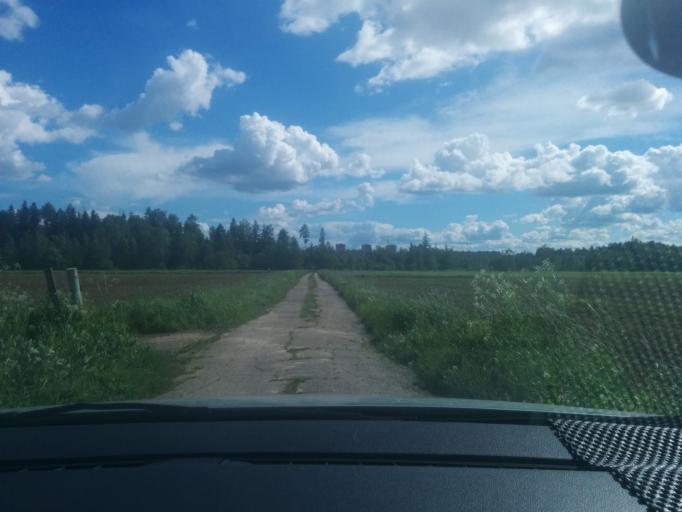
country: RU
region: Moskovskaya
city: Lugovaya
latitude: 56.0413
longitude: 37.4969
